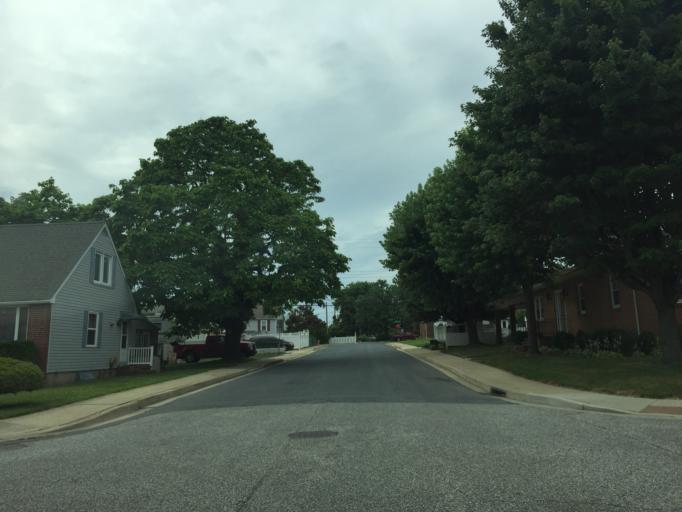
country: US
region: Maryland
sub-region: Baltimore County
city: Edgemere
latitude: 39.2399
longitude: -76.4538
